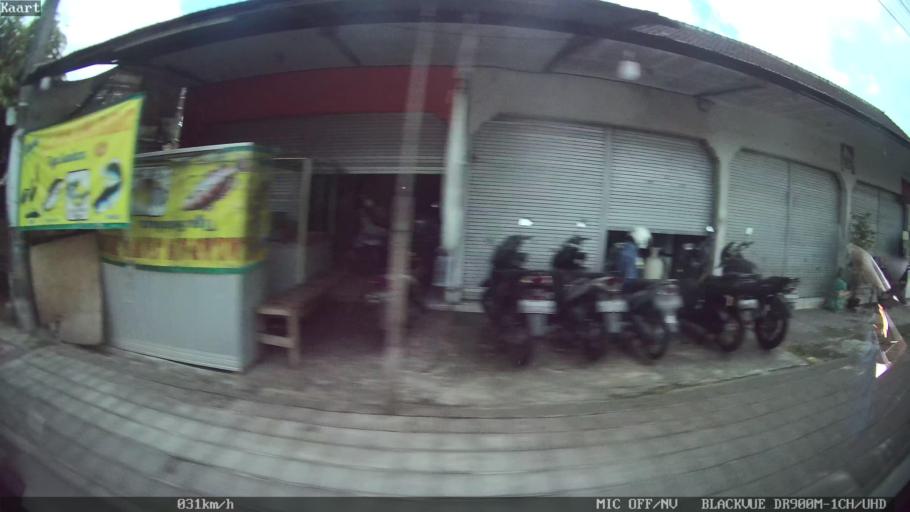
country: ID
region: Bali
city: Banjar Pekenjelodan
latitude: -8.5915
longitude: 115.1763
